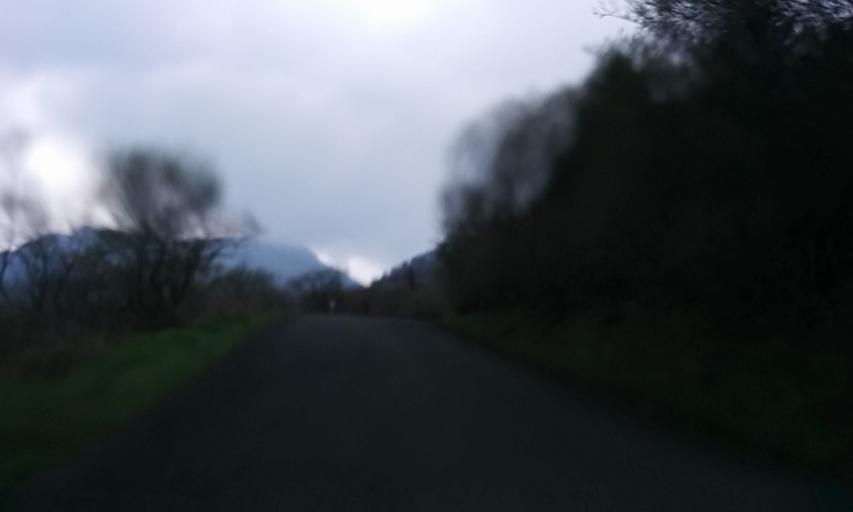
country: JP
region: Ehime
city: Saijo
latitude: 33.7862
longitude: 133.2139
